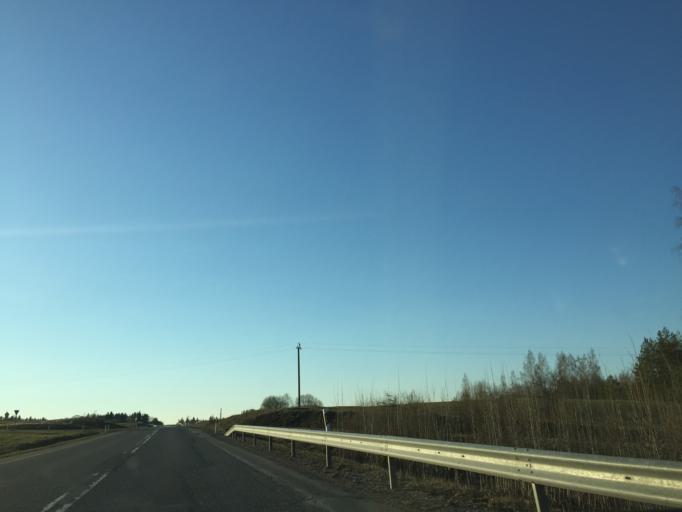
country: EE
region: Ida-Virumaa
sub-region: Johvi vald
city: Johvi
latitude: 59.1919
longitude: 27.5560
